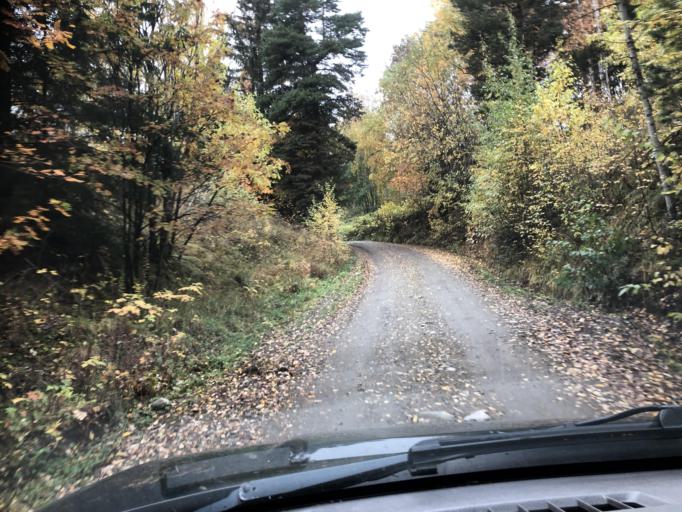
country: NO
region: Oppland
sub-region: Sor-Fron
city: Hundorp
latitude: 61.5727
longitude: 9.9150
